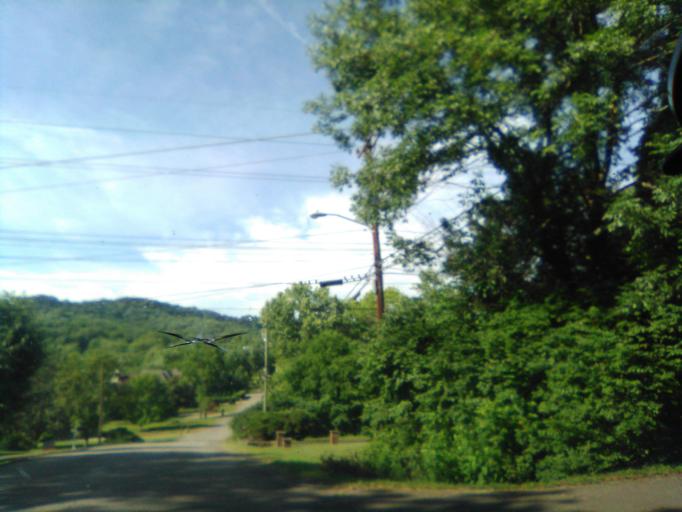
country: US
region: Tennessee
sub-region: Davidson County
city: Belle Meade
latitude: 36.1192
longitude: -86.9058
